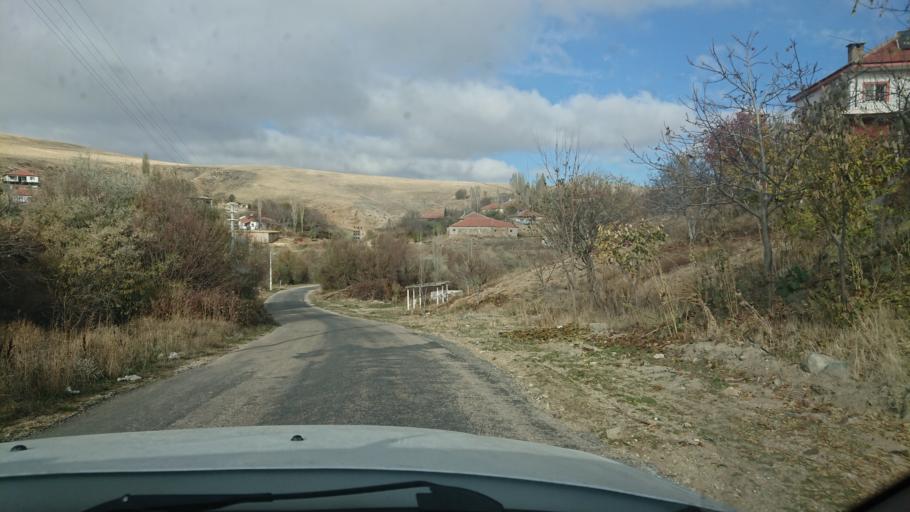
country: TR
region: Aksaray
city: Ortakoy
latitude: 38.8041
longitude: 33.9835
